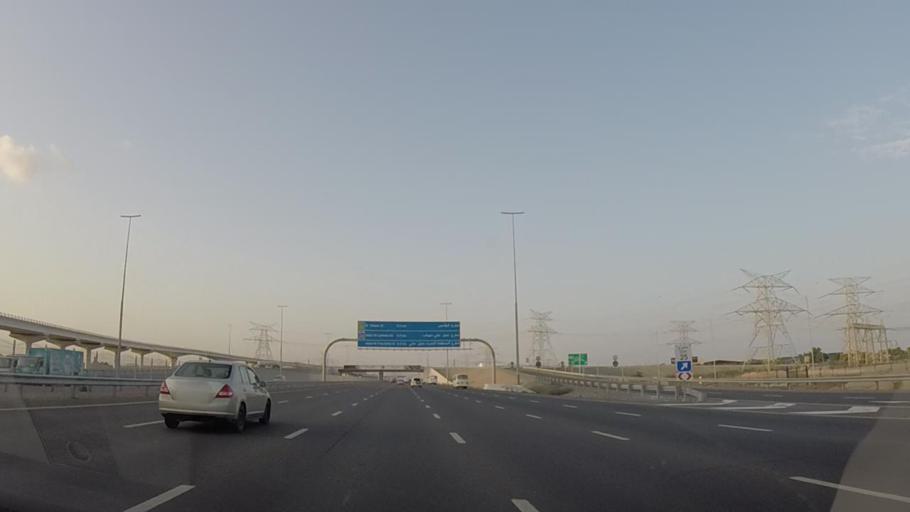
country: AE
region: Dubai
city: Dubai
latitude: 25.0427
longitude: 55.1131
